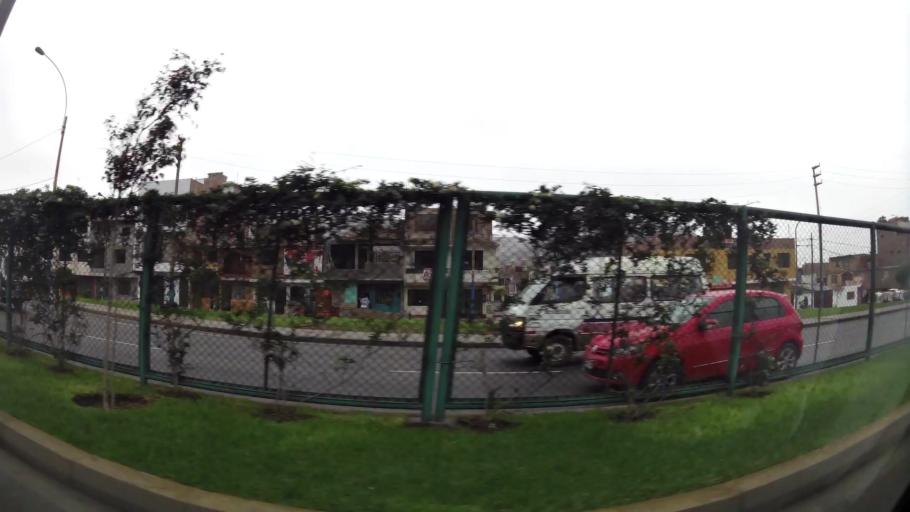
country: PE
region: Lima
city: Ventanilla
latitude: -11.8987
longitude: -77.1274
